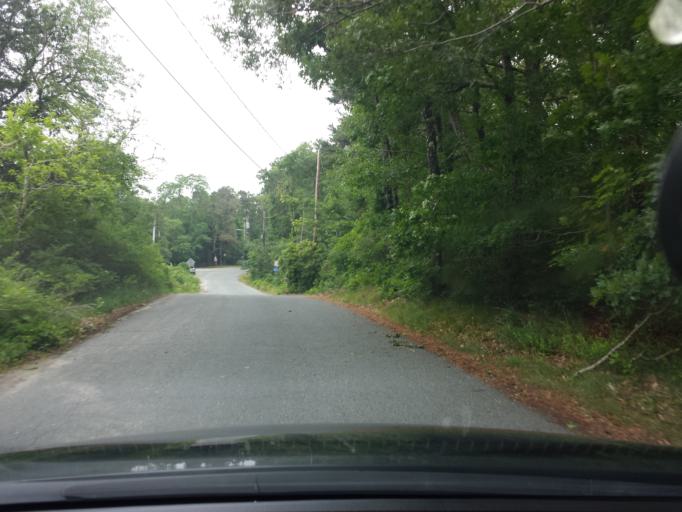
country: US
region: Massachusetts
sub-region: Barnstable County
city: Marstons Mills
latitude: 41.6462
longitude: -70.4120
